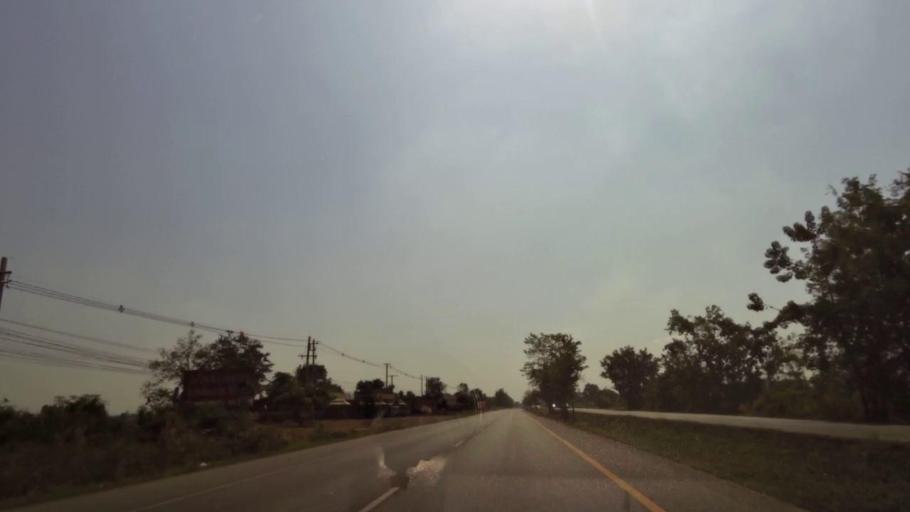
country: TH
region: Phichit
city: Bueng Na Rang
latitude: 16.3054
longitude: 100.1285
